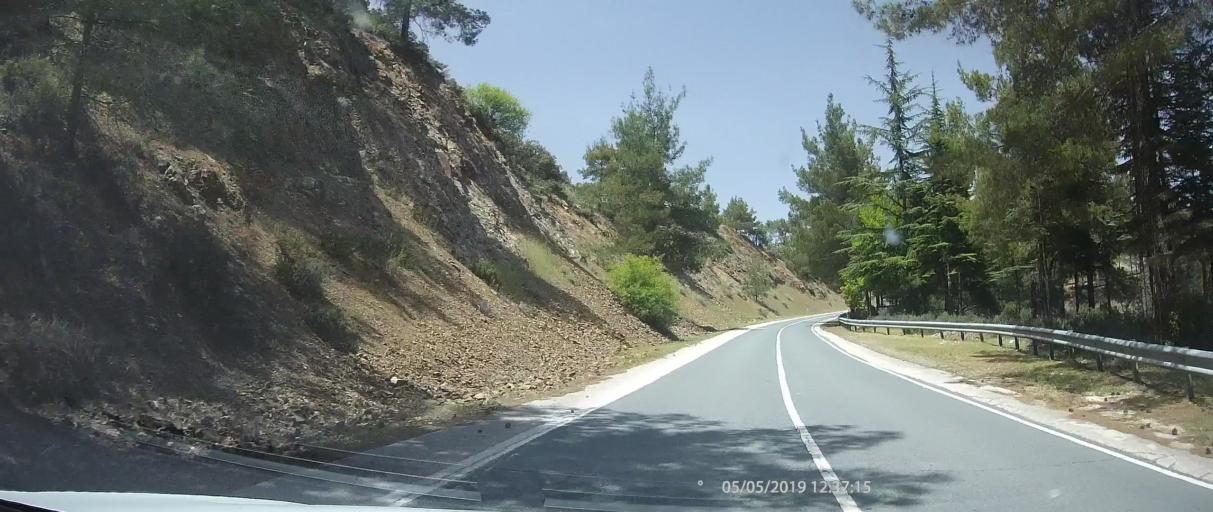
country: CY
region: Lefkosia
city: Kakopetria
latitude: 34.9840
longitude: 32.7862
